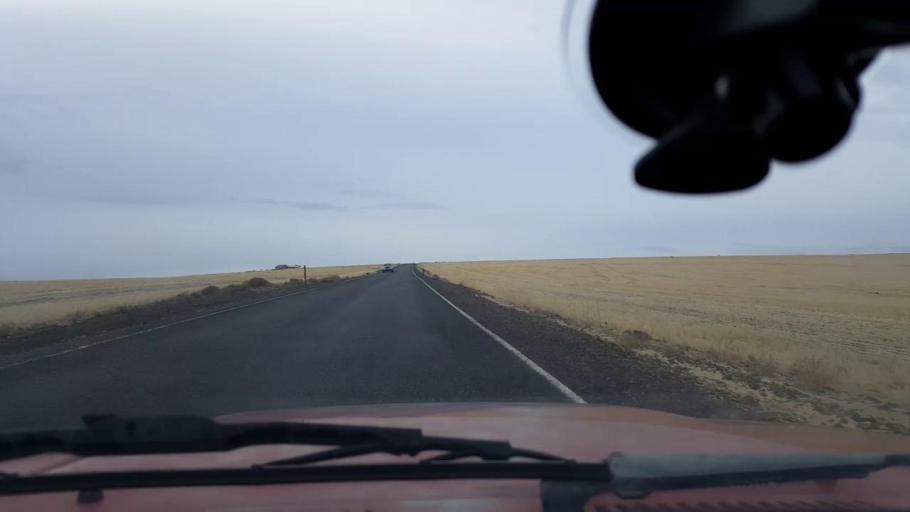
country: US
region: Washington
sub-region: Asotin County
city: Clarkston Heights-Vineland
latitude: 46.3433
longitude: -117.2656
